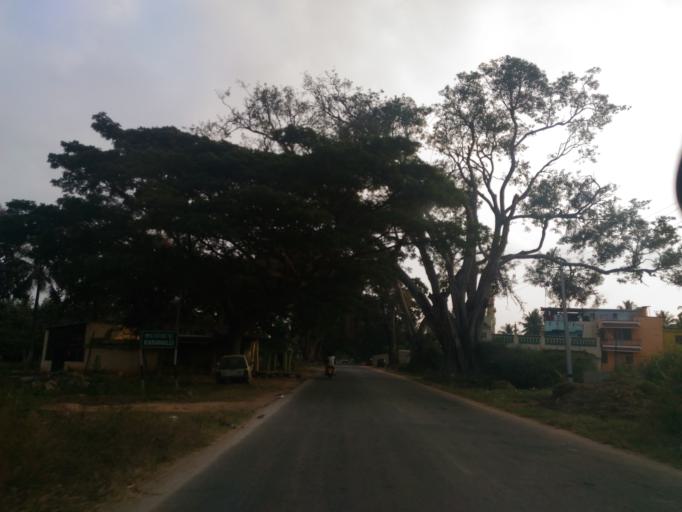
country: IN
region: Karnataka
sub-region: Bangalore Rural
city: Devanhalli
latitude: 13.3307
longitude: 77.6911
